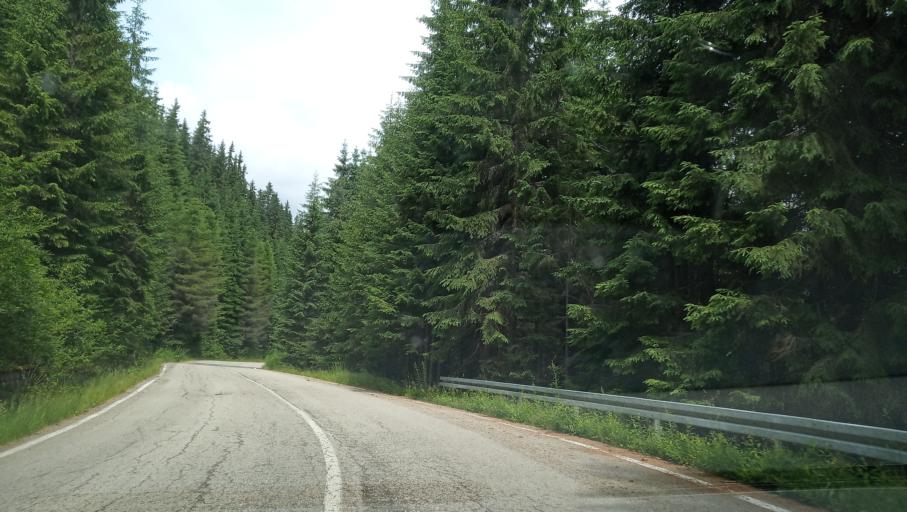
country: RO
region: Valcea
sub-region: Comuna Voineasa
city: Voineasa
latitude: 45.4211
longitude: 23.7536
